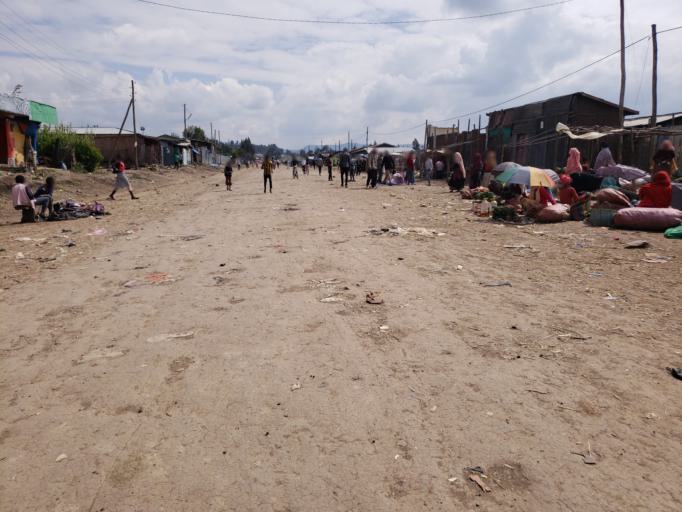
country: ET
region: Oromiya
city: Dodola
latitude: 7.0057
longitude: 39.3917
